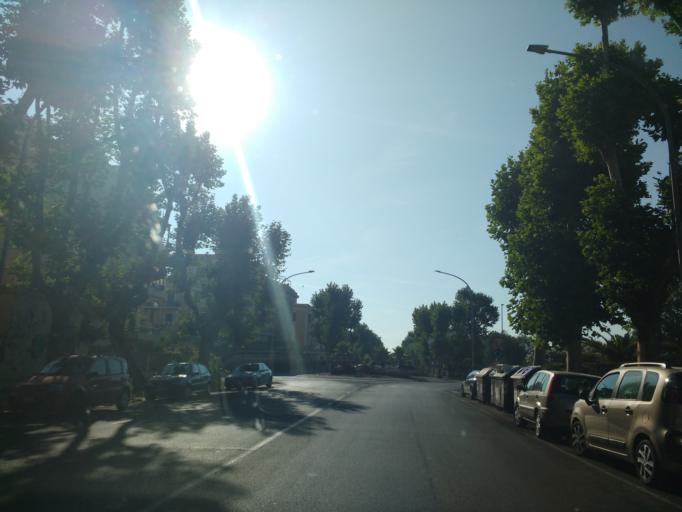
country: IT
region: Latium
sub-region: Citta metropolitana di Roma Capitale
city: Lido di Ostia
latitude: 41.7272
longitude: 12.2877
